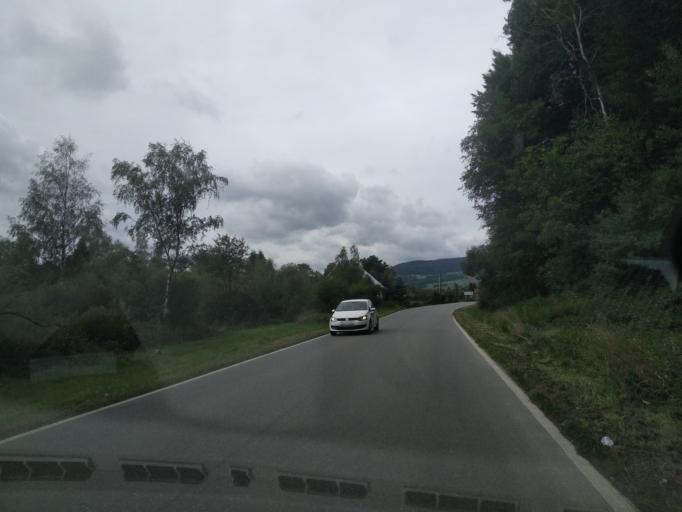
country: PL
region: Lesser Poland Voivodeship
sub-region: Powiat gorlicki
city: Ropa
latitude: 49.5752
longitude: 21.0735
